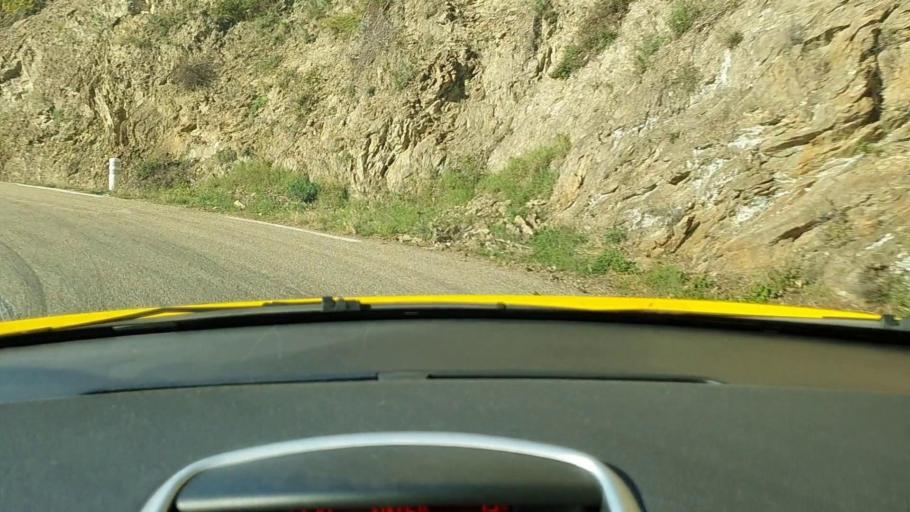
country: FR
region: Languedoc-Roussillon
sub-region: Departement du Gard
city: Sumene
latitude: 43.9887
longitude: 3.6966
